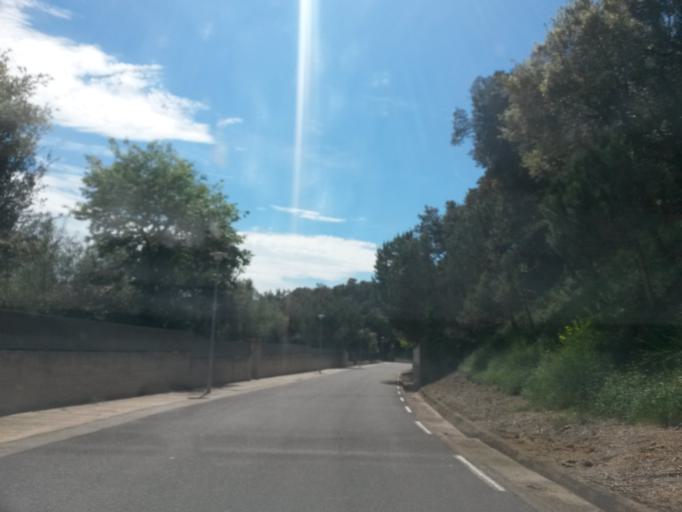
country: ES
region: Catalonia
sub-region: Provincia de Girona
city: Vilablareix
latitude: 41.9651
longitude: 2.7592
